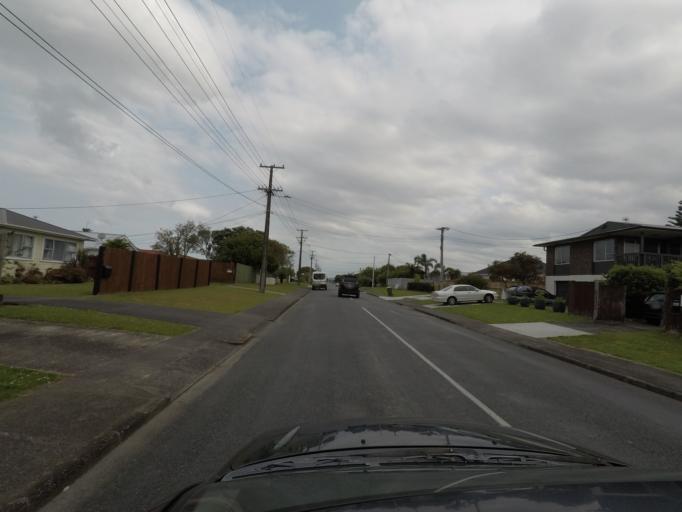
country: NZ
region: Auckland
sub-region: Auckland
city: Rosebank
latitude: -36.8270
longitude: 174.6465
